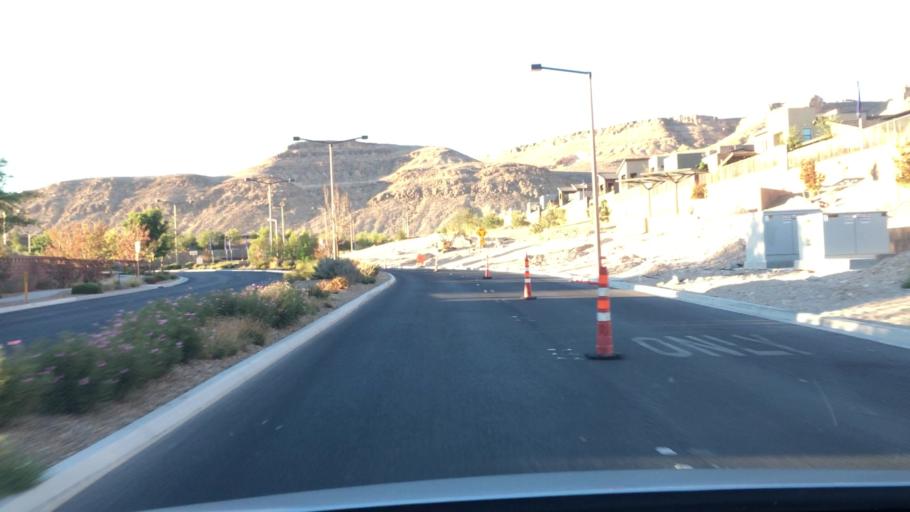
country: US
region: Nevada
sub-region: Clark County
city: Summerlin South
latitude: 36.0685
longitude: -115.3159
